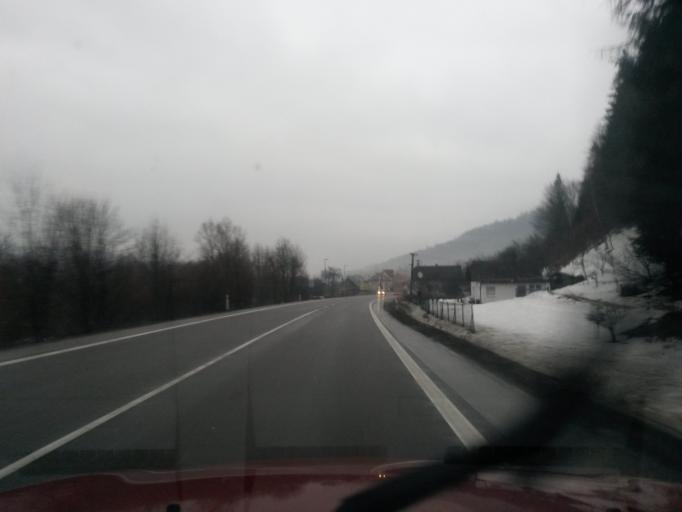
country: SK
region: Zilinsky
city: Kysucke Nove Mesto
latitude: 49.3103
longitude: 18.8012
